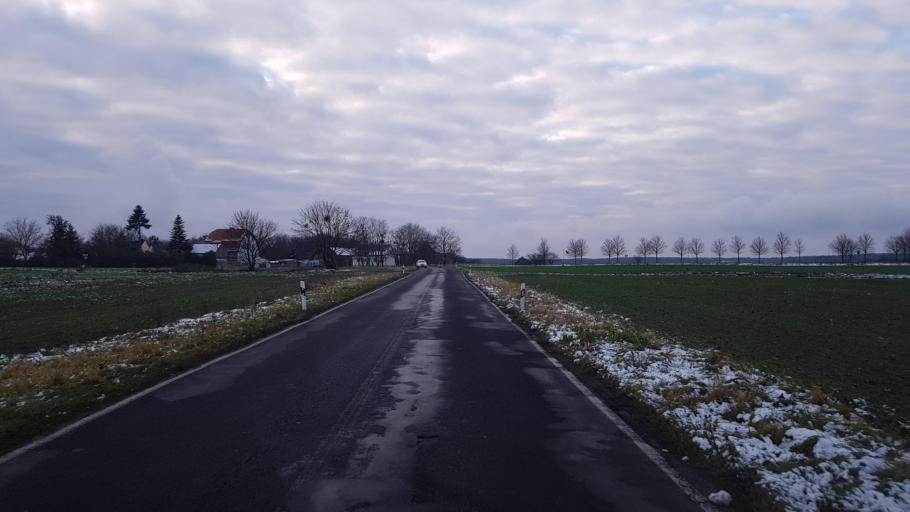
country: DE
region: Brandenburg
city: Rehfelde
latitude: 52.5180
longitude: 13.9017
